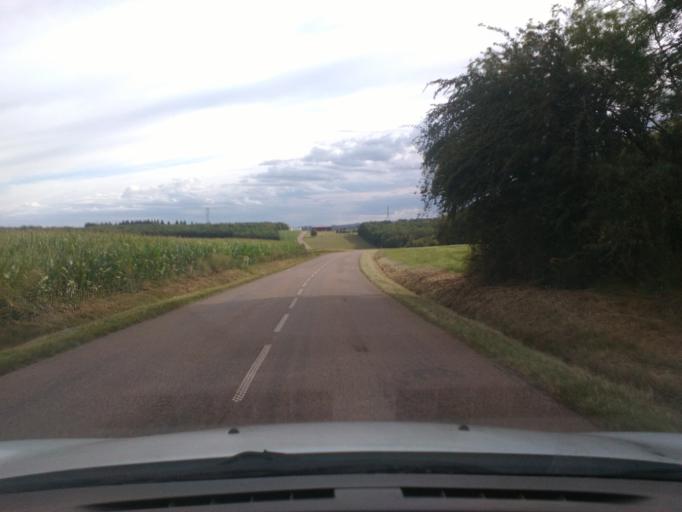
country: FR
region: Lorraine
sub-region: Departement des Vosges
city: Chatel-sur-Moselle
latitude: 48.3315
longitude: 6.4146
